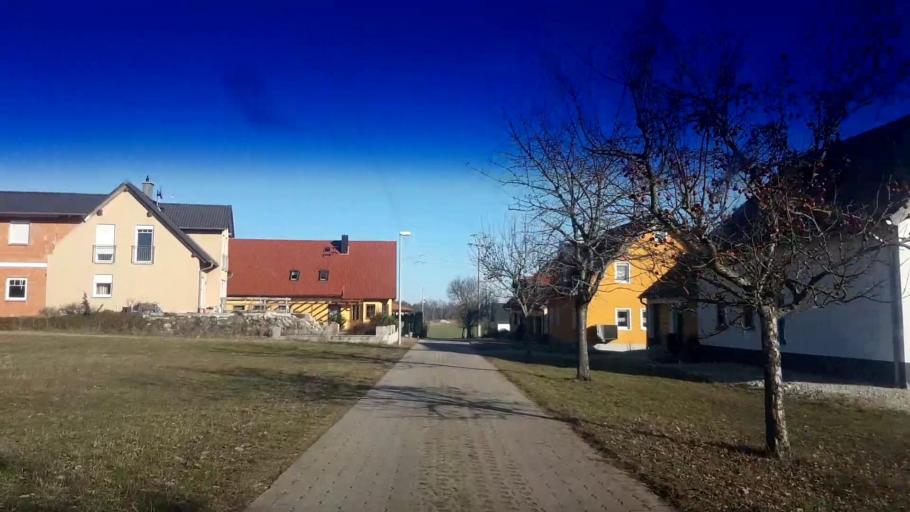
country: DE
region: Bavaria
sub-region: Upper Franconia
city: Poxdorf
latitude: 49.9619
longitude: 11.1016
